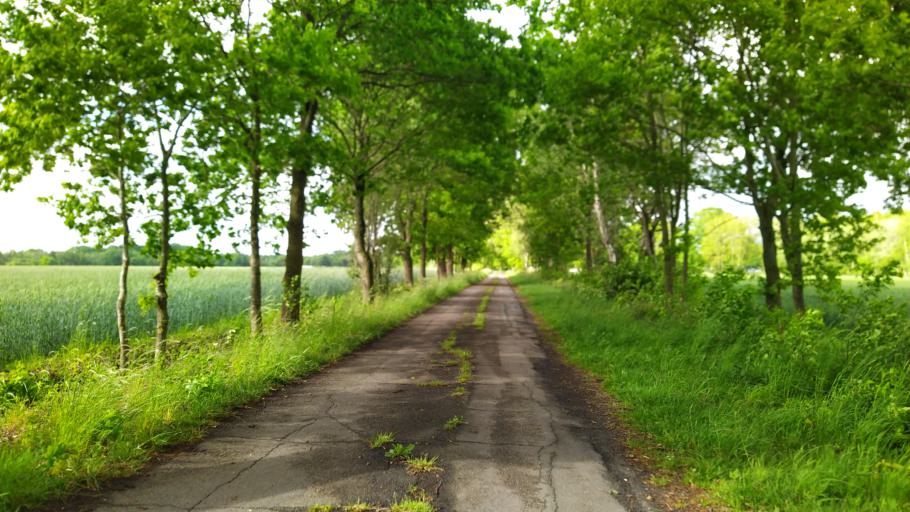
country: DE
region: Lower Saxony
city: Farven
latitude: 53.4257
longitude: 9.3525
